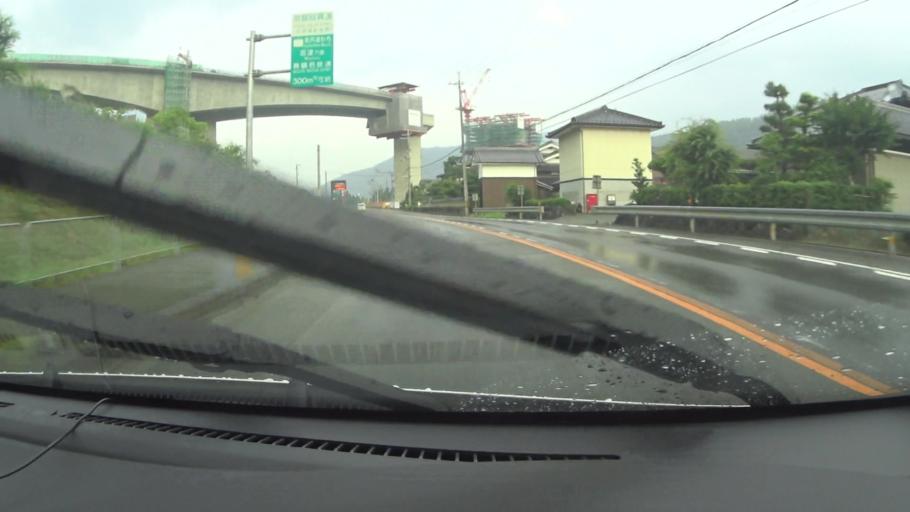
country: JP
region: Kyoto
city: Ayabe
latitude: 35.2774
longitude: 135.3365
